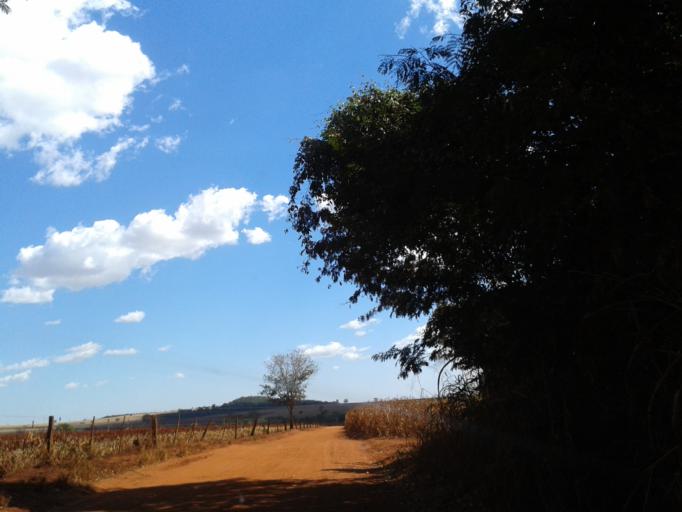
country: BR
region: Minas Gerais
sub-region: Capinopolis
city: Capinopolis
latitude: -18.6199
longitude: -49.4910
